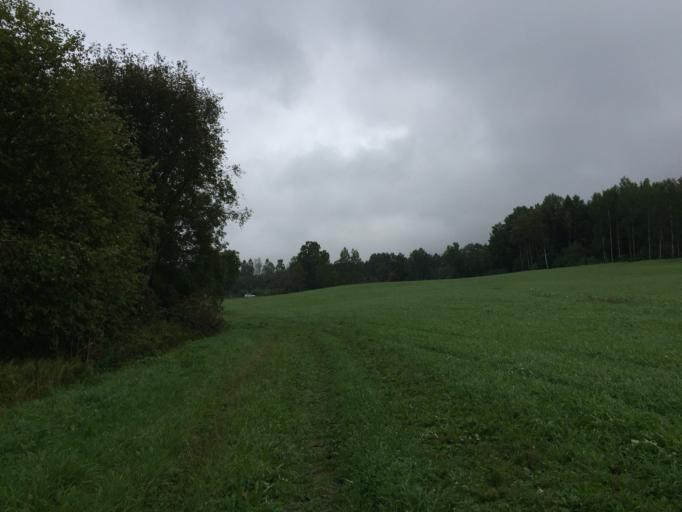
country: NO
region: Akershus
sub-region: Baerum
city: Lysaker
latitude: 59.9824
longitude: 10.6197
